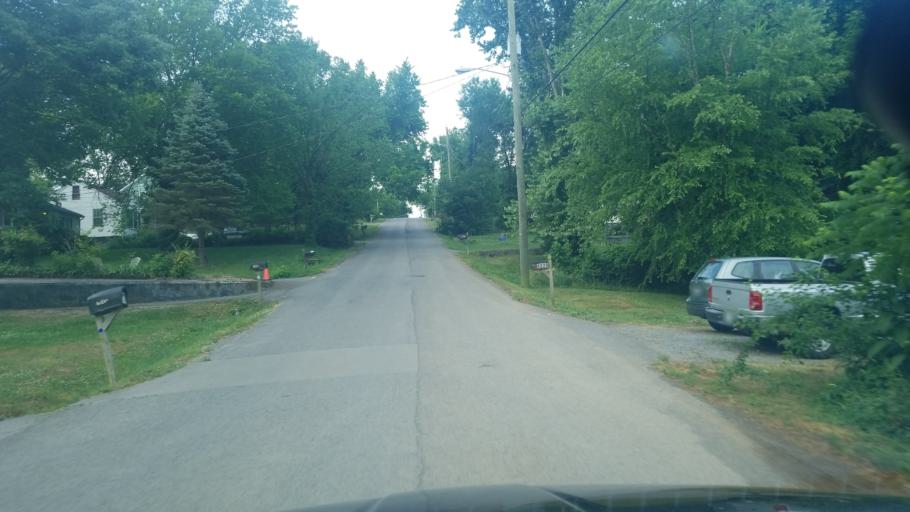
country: US
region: Tennessee
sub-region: Davidson County
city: Nashville
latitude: 36.2253
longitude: -86.7387
